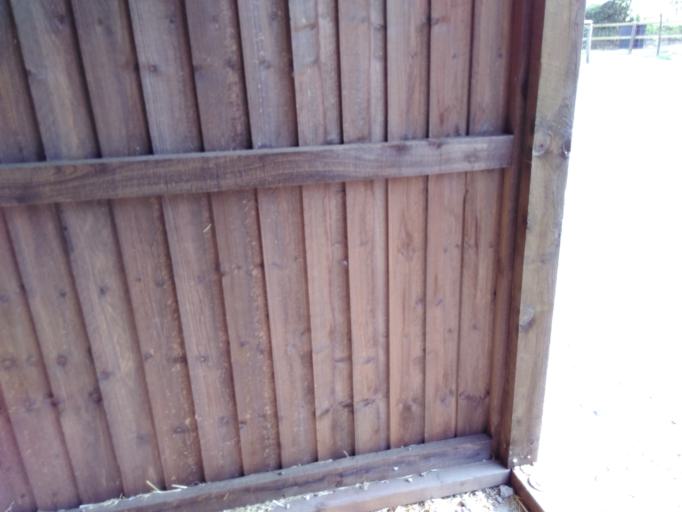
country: GB
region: England
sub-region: Suffolk
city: Ipswich
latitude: 52.0199
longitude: 1.1250
